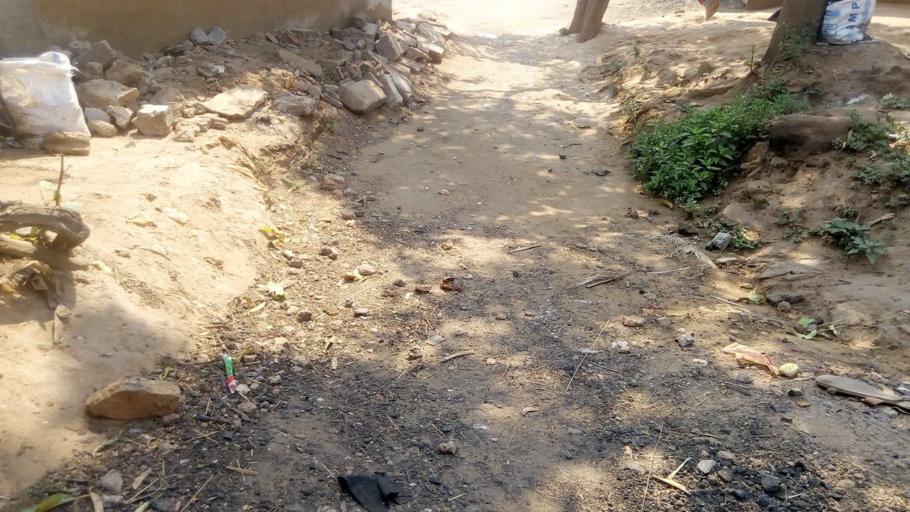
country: ZM
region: Lusaka
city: Lusaka
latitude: -15.3570
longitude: 28.2955
